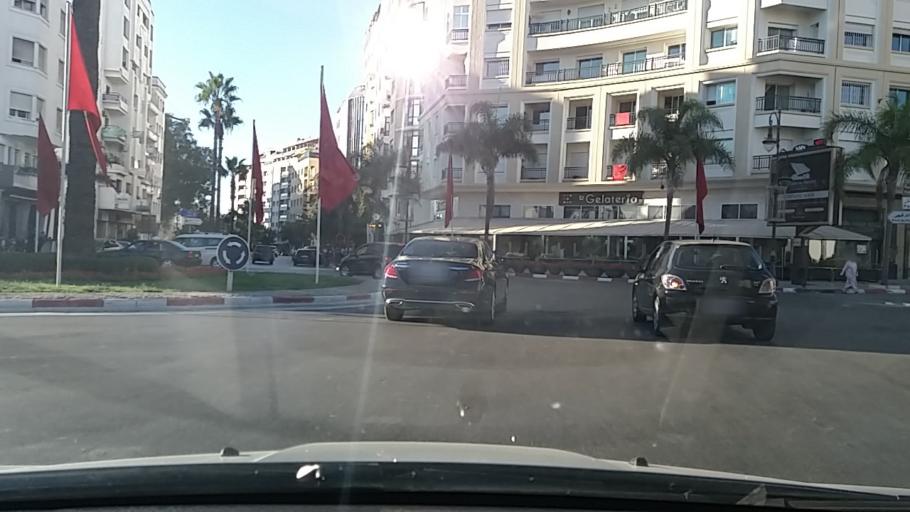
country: MA
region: Tanger-Tetouan
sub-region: Tanger-Assilah
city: Tangier
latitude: 35.7812
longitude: -5.8207
